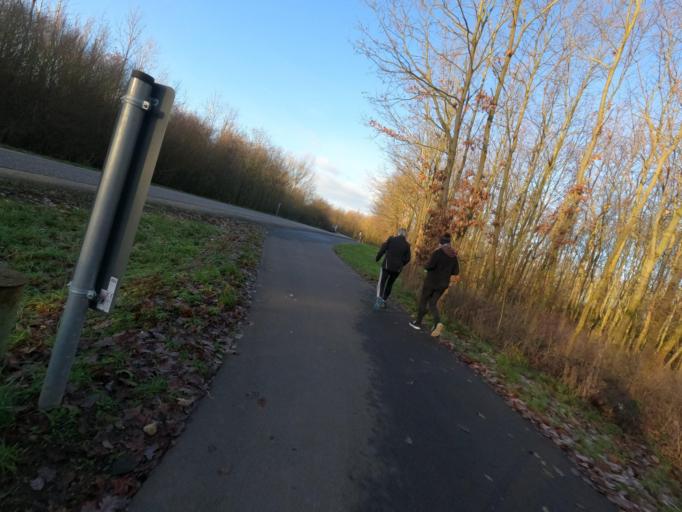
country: DE
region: North Rhine-Westphalia
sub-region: Regierungsbezirk Koln
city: Elsdorf
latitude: 50.9350
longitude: 6.5386
